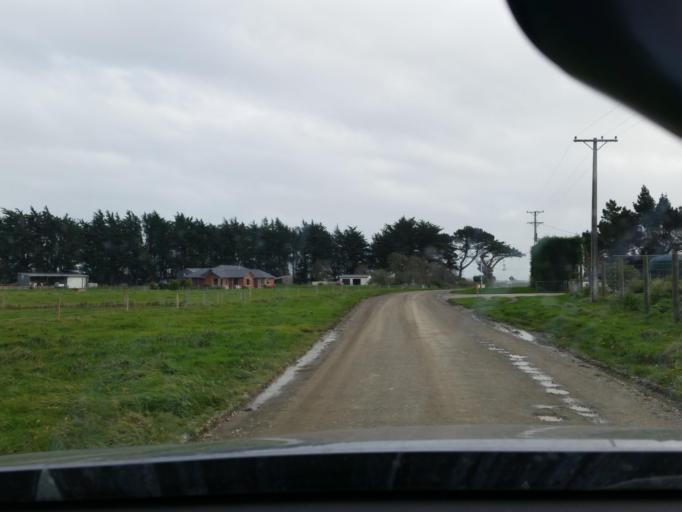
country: NZ
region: Southland
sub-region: Invercargill City
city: Invercargill
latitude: -46.3296
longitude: 168.3401
